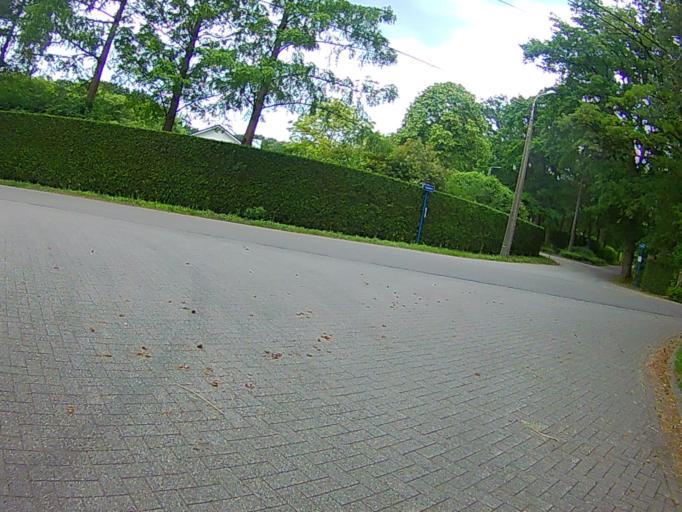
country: BE
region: Flanders
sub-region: Provincie Vlaams-Brabant
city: Keerbergen
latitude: 50.9925
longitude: 4.6488
